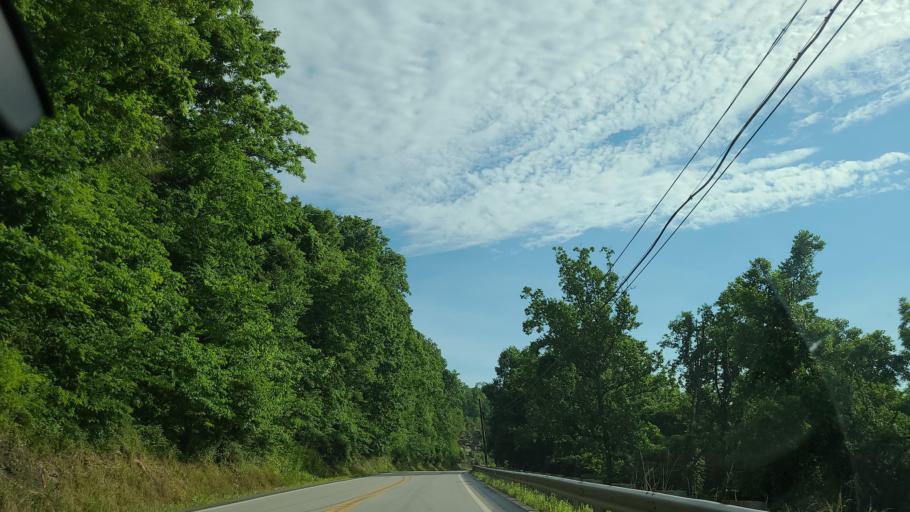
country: US
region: Kentucky
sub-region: Whitley County
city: Williamsburg
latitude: 36.7258
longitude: -84.1265
